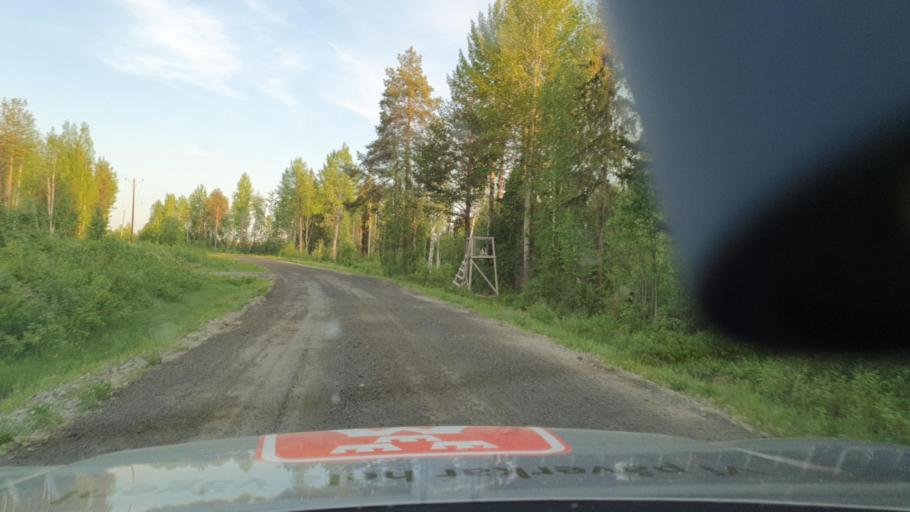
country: SE
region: Norrbotten
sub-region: Bodens Kommun
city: Boden
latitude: 66.1156
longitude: 21.5585
